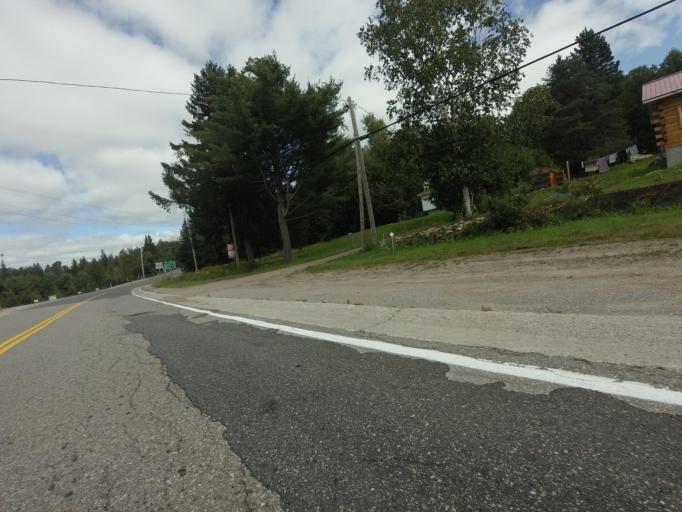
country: CA
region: Ontario
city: Bancroft
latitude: 44.9722
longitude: -78.2753
